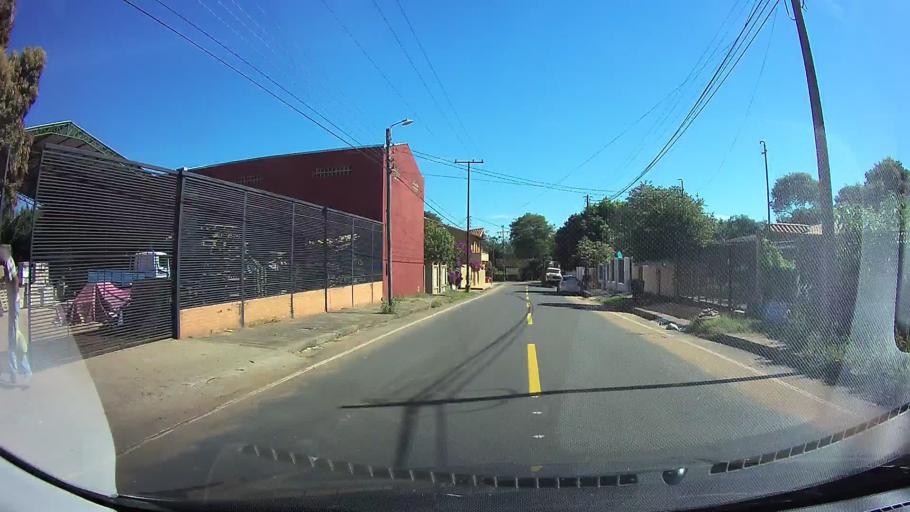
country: PY
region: Central
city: San Lorenzo
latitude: -25.2692
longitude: -57.4740
